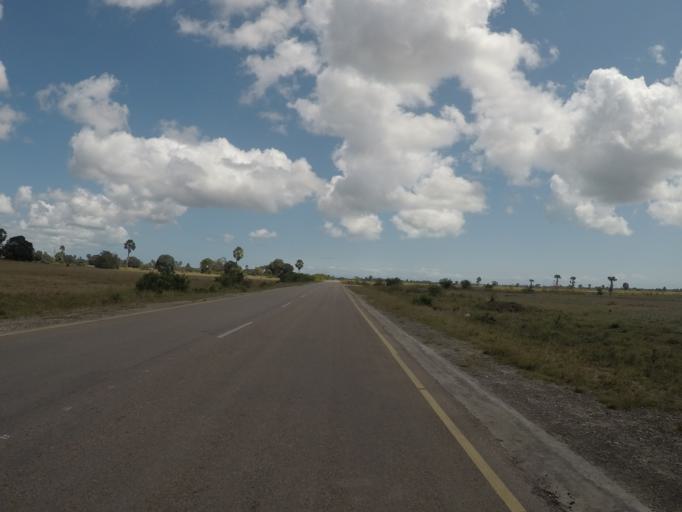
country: TZ
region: Zanzibar Central/South
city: Koani
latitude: -6.2010
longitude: 39.3690
